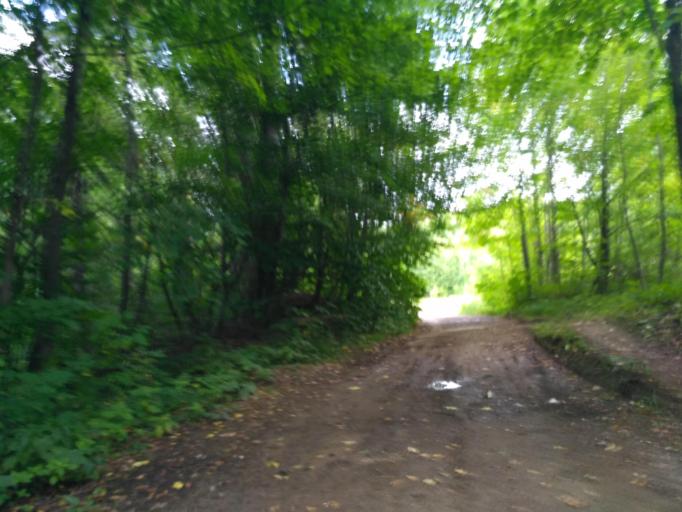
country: PL
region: Subcarpathian Voivodeship
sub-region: Powiat krosnienski
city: Iwonicz-Zdroj
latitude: 49.5703
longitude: 21.8076
